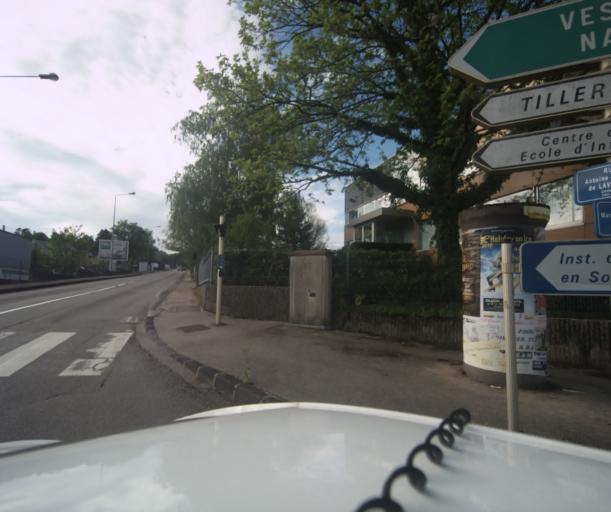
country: FR
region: Franche-Comte
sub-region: Departement du Doubs
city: Pirey
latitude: 47.2356
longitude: 5.9827
